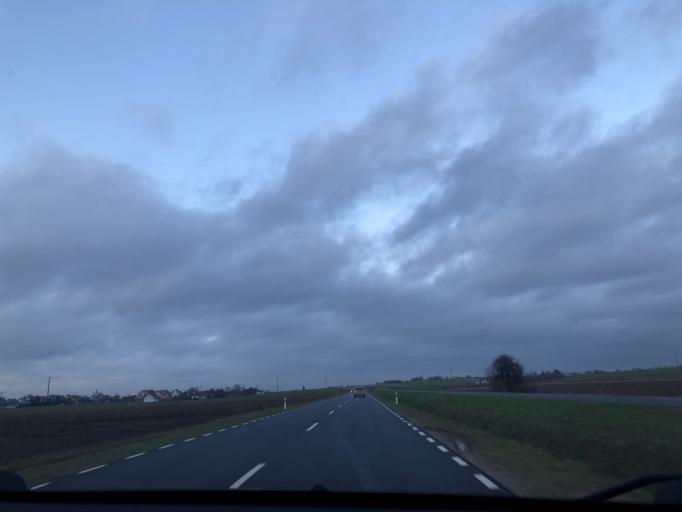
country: PL
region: Podlasie
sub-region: Lomza
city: Lomza
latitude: 53.1393
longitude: 22.0512
